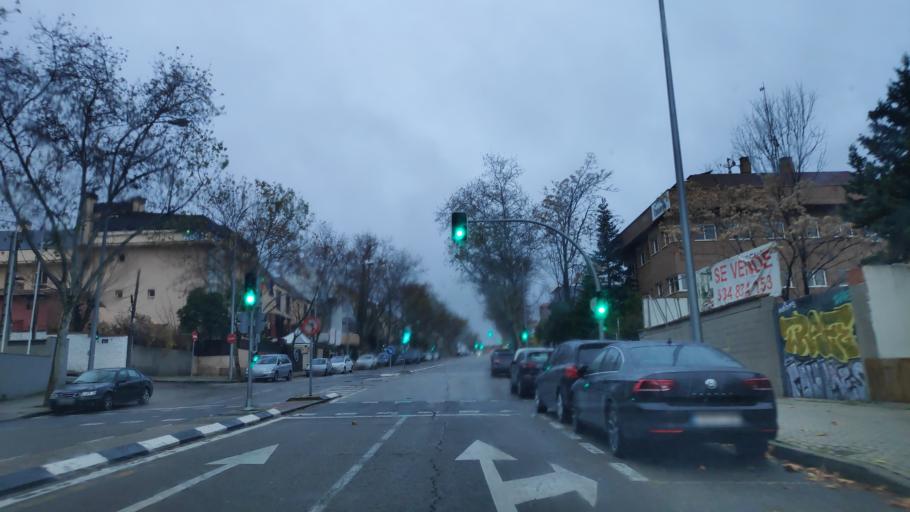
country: ES
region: Madrid
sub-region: Provincia de Madrid
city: Ciudad Lineal
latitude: 40.4572
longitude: -3.6474
